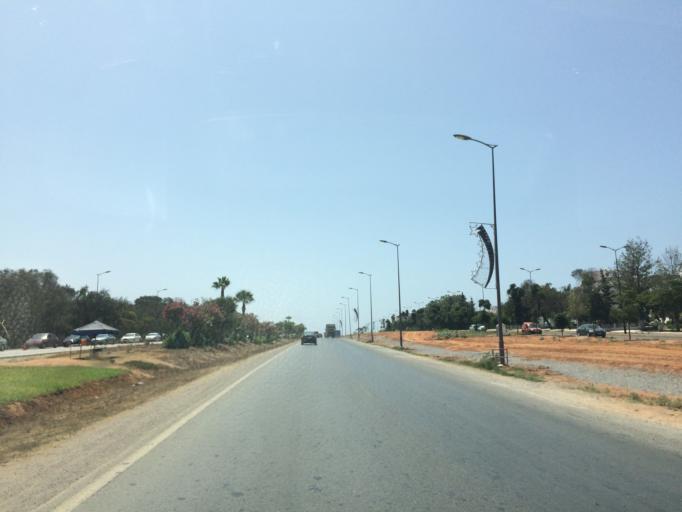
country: MA
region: Rabat-Sale-Zemmour-Zaer
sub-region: Skhirate-Temara
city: Temara
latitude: 33.9666
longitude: -6.8890
